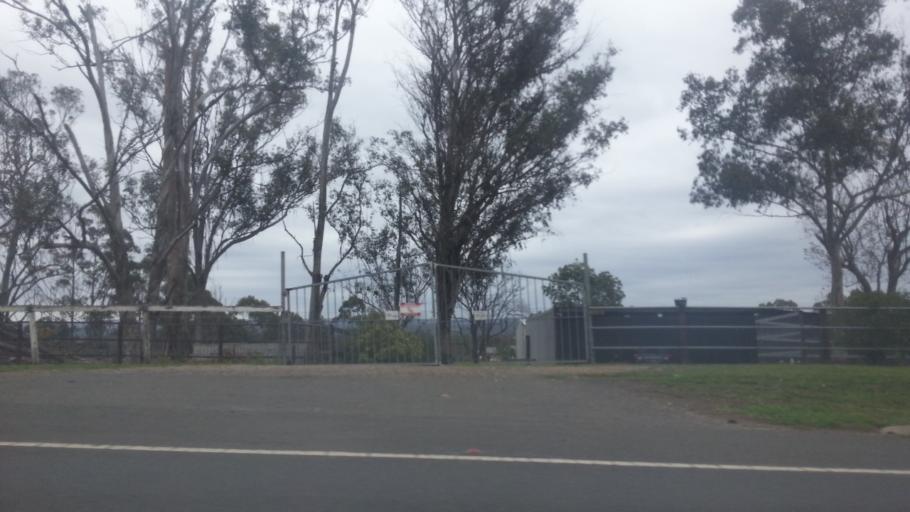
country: AU
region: New South Wales
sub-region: Penrith Municipality
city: Mulgoa
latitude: -33.8377
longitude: 150.6832
